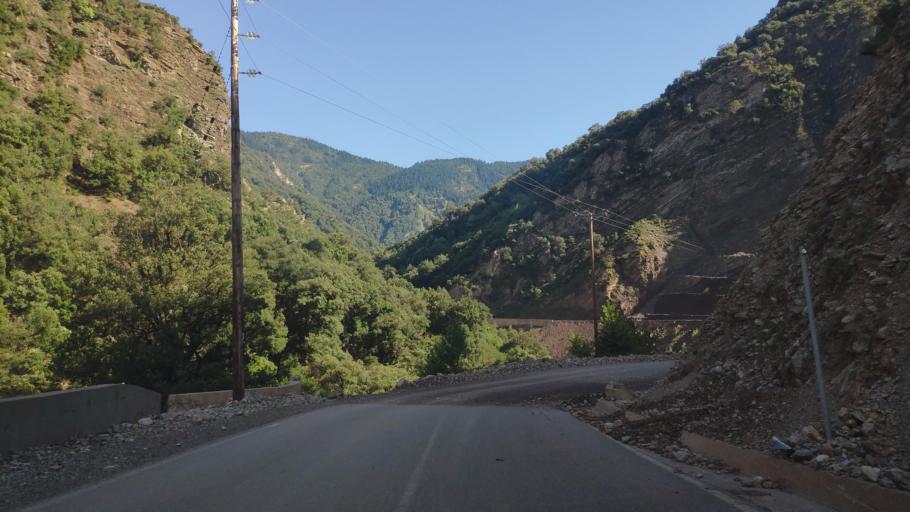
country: GR
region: Central Greece
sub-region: Nomos Evrytanias
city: Kerasochori
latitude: 39.0732
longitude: 21.6010
